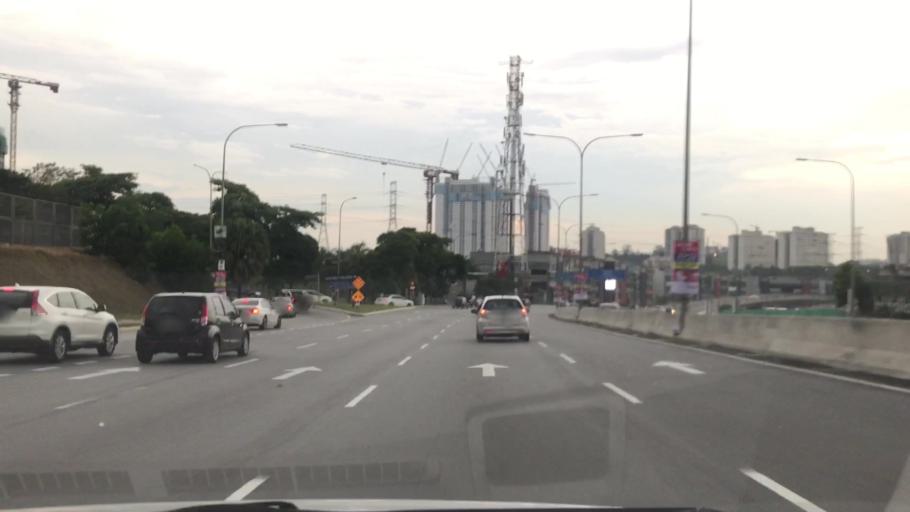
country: MY
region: Selangor
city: Kampong Baharu Balakong
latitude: 3.0488
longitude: 101.6740
